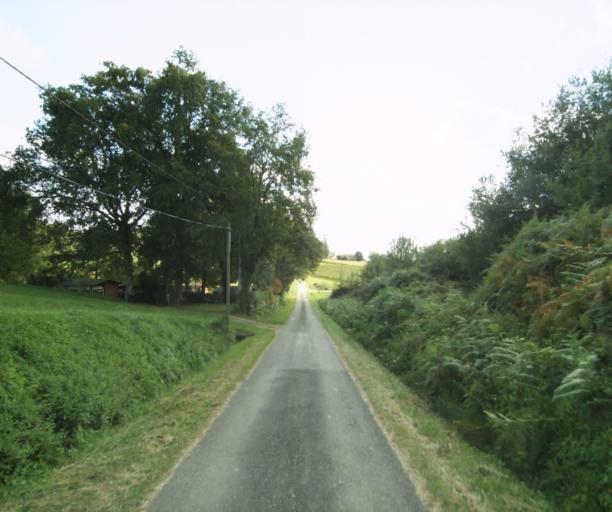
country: FR
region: Midi-Pyrenees
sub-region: Departement du Gers
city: Cazaubon
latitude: 43.9307
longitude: -0.0557
